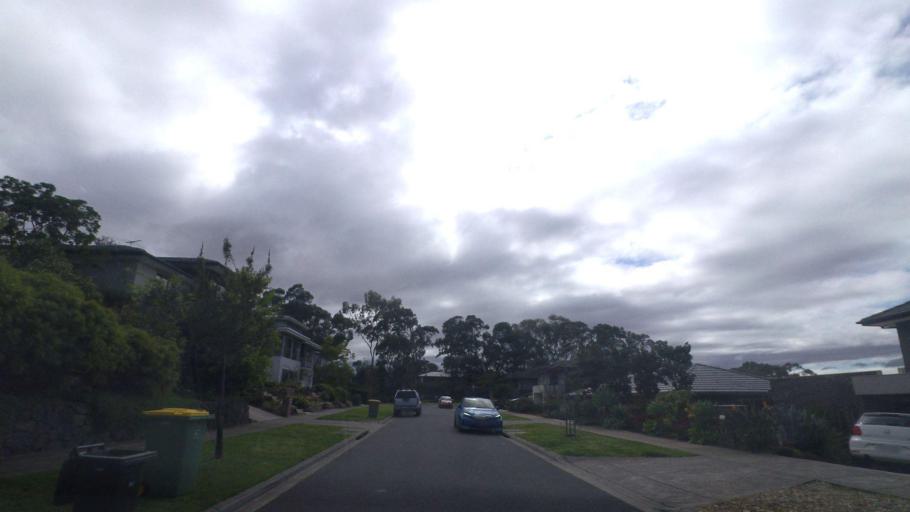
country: AU
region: Victoria
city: Watsonia
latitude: -37.7145
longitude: 145.0678
